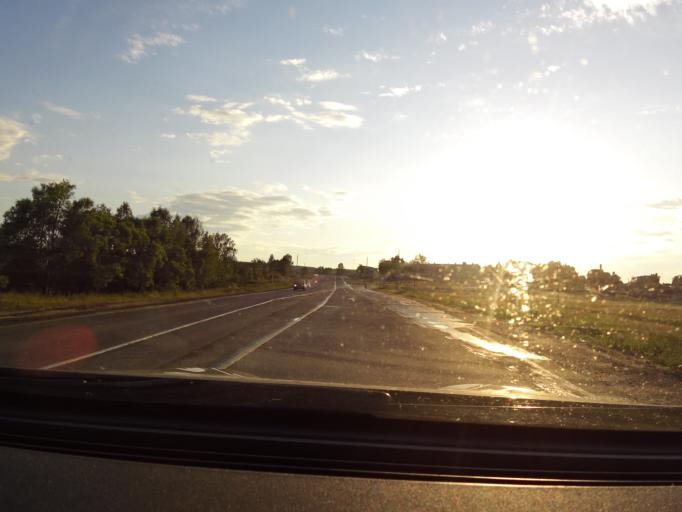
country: RU
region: Vladimir
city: Belaya Rechka
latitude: 56.2809
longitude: 39.4166
